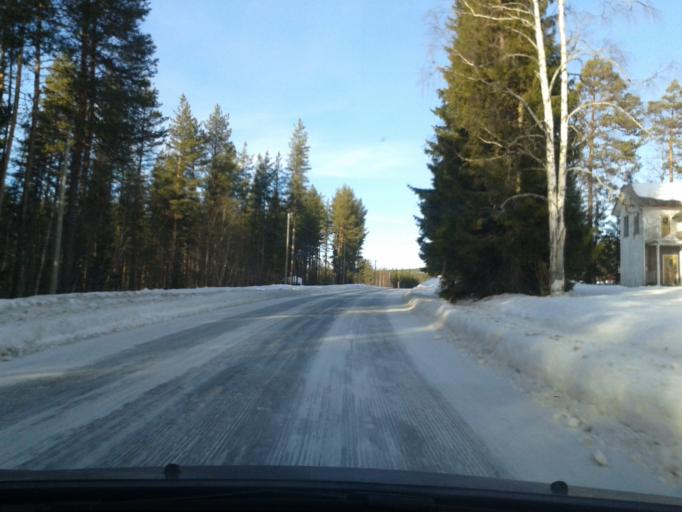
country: SE
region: Vaesternorrland
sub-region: OErnskoeldsviks Kommun
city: Bredbyn
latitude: 63.7346
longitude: 17.7439
